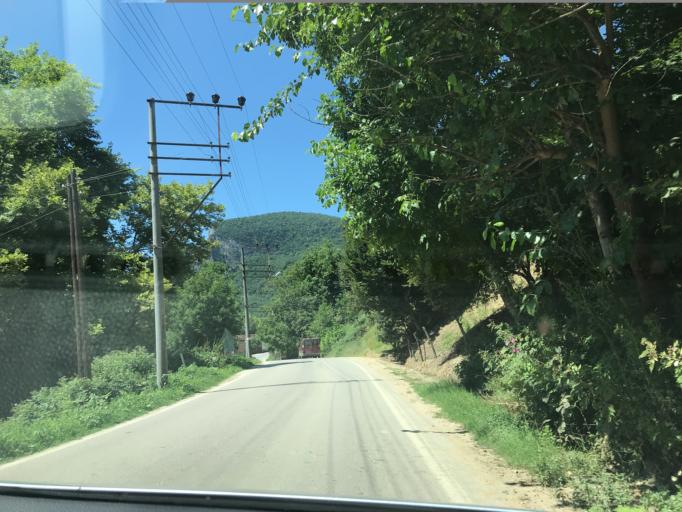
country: TR
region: Bursa
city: Tahtakopru
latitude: 39.9534
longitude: 29.5997
